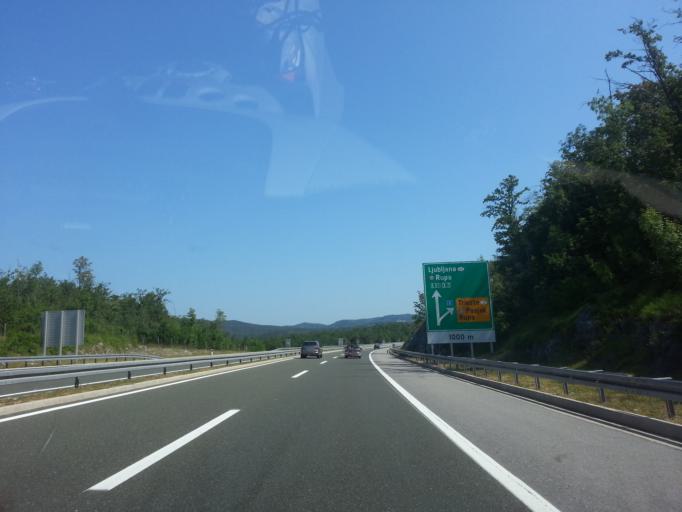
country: HR
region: Primorsko-Goranska
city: Klana
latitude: 45.4585
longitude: 14.2686
